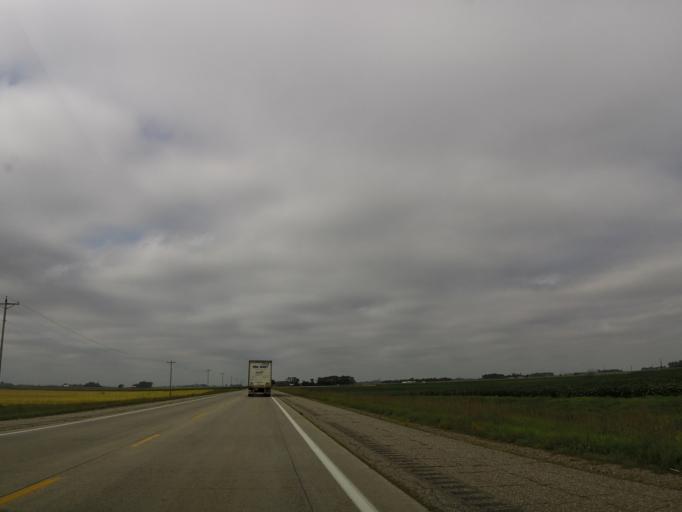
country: US
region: Minnesota
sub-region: Renville County
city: Bird Island
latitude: 44.7676
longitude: -94.9272
